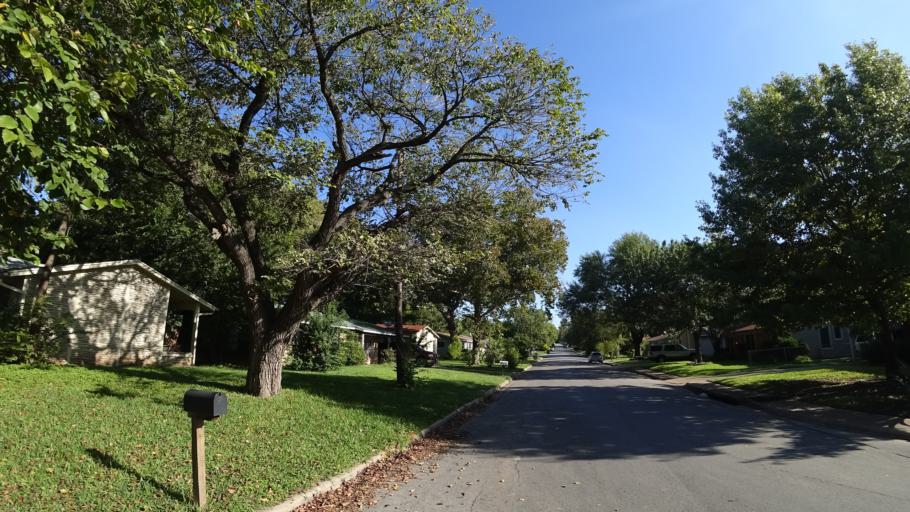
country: US
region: Texas
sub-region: Travis County
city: Wells Branch
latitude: 30.3562
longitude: -97.6976
